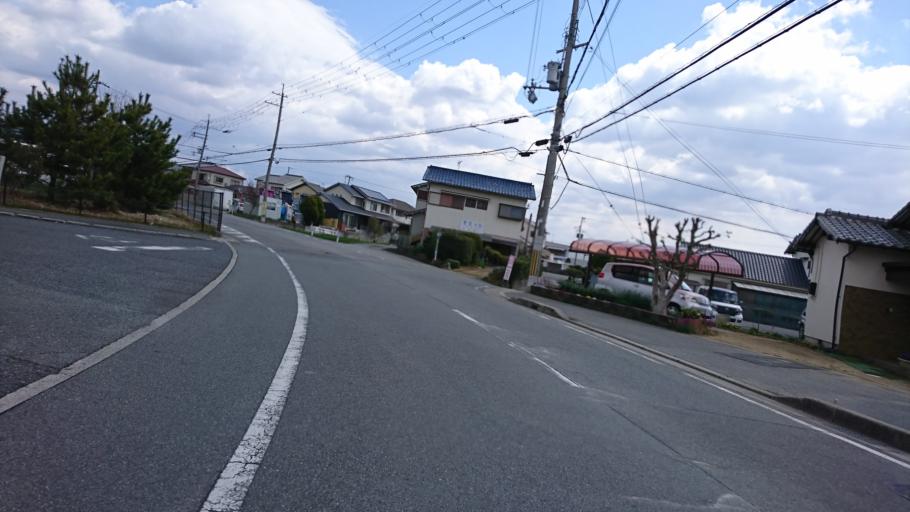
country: JP
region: Hyogo
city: Kakogawacho-honmachi
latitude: 34.7710
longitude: 134.8680
